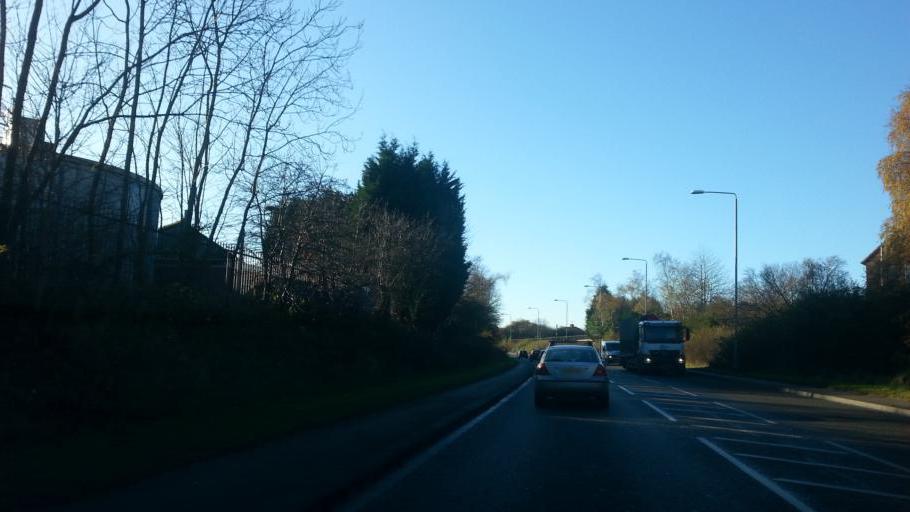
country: GB
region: England
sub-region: Nottinghamshire
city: Sutton in Ashfield
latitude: 53.1191
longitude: -1.2534
